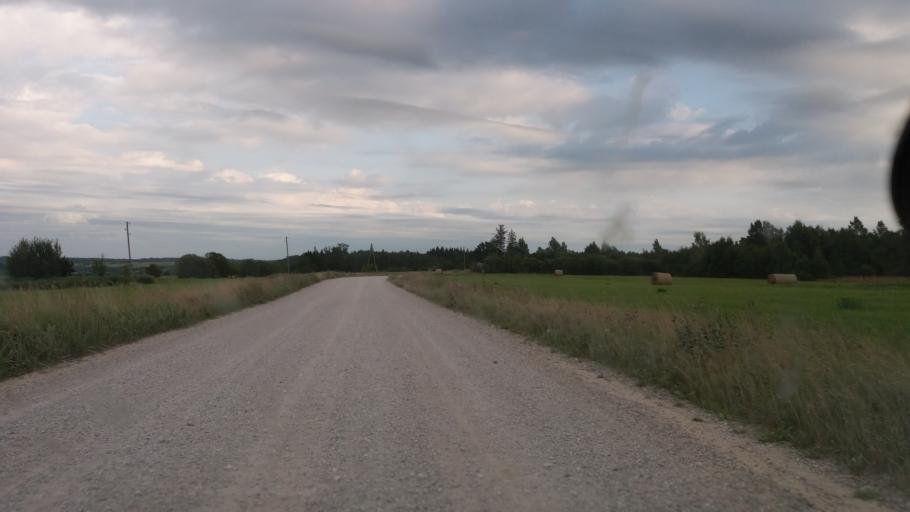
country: LV
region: Talsu Rajons
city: Sabile
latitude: 57.0258
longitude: 22.5839
